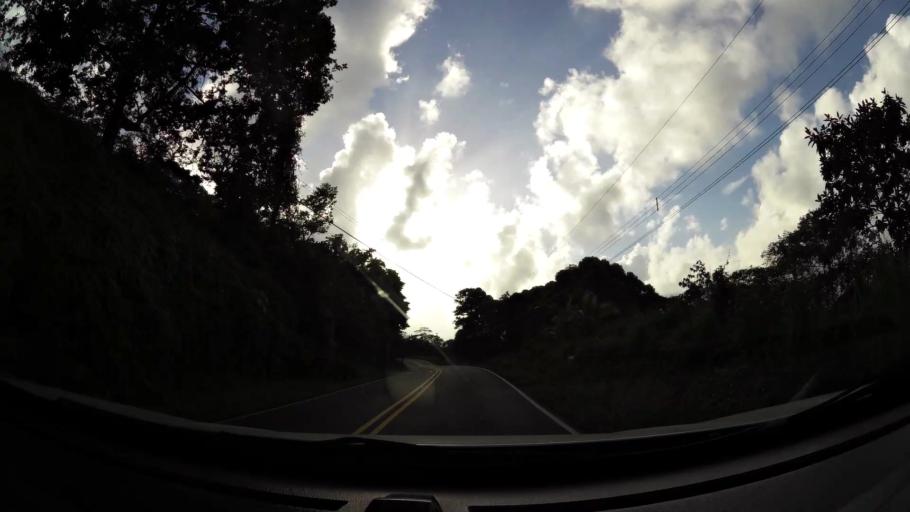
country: CR
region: Limon
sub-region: Canton de Siquirres
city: Siquirres
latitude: 10.0757
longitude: -83.5494
